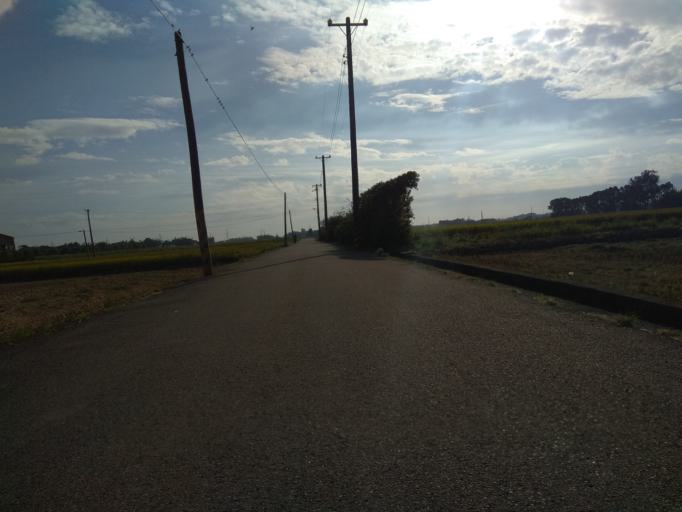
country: TW
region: Taiwan
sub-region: Hsinchu
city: Zhubei
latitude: 24.9812
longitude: 121.0479
